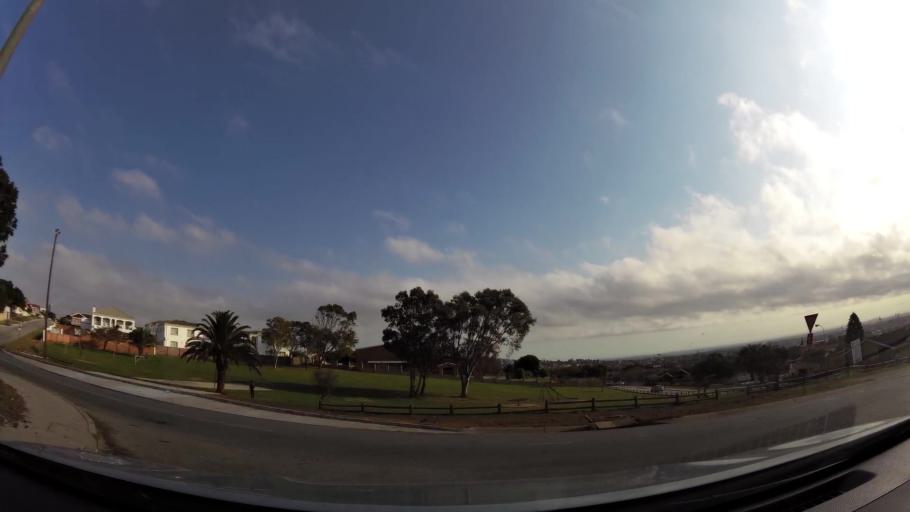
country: ZA
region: Eastern Cape
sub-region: Nelson Mandela Bay Metropolitan Municipality
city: Port Elizabeth
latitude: -33.9247
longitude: 25.5562
